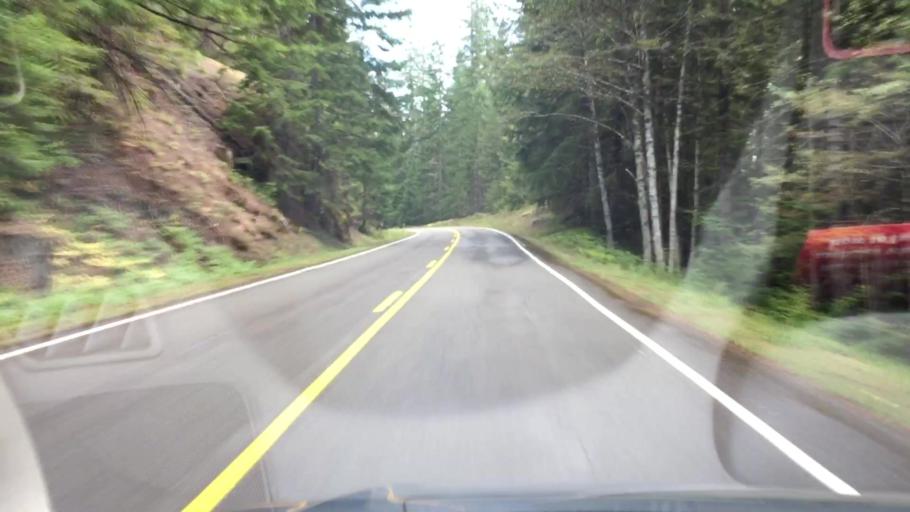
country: US
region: Washington
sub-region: Pierce County
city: Buckley
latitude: 46.7558
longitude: -121.6249
